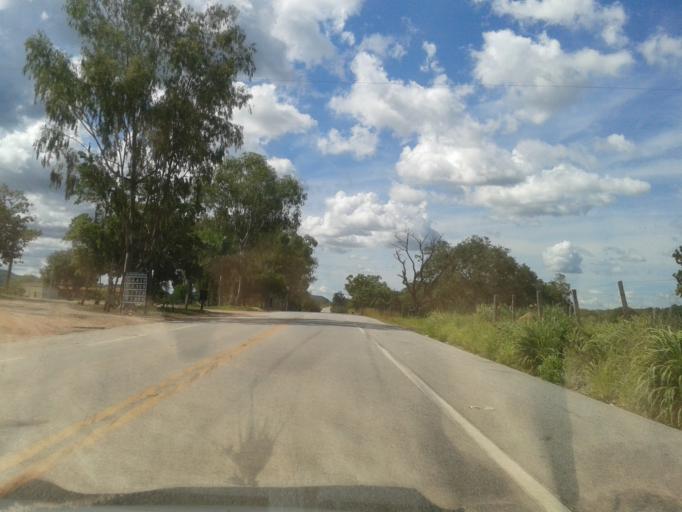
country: BR
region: Goias
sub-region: Itapuranga
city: Itapuranga
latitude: -15.5743
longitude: -50.2750
